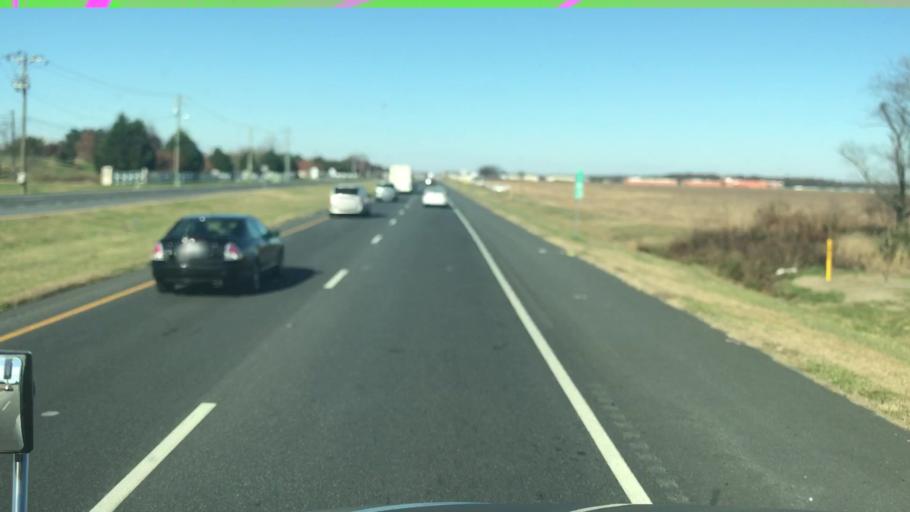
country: US
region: Delaware
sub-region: Sussex County
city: Bridgeville
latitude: 38.7086
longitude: -75.5883
